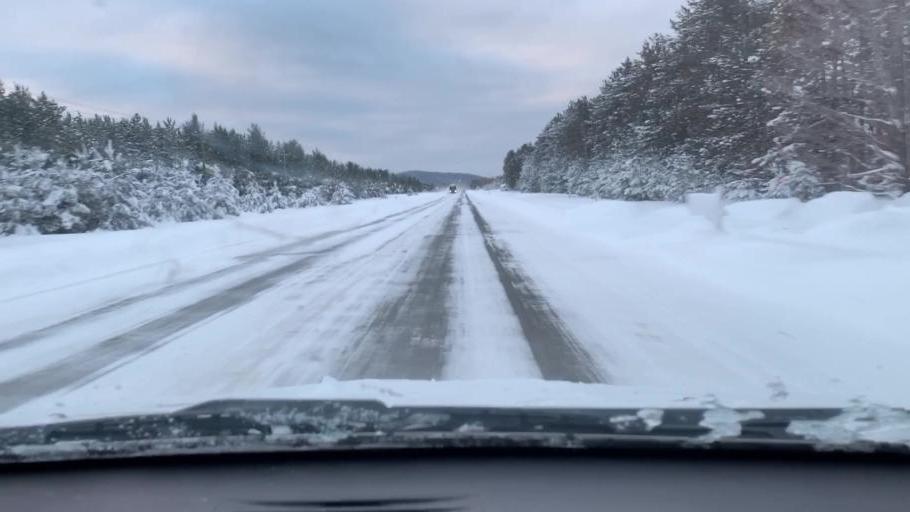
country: US
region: Michigan
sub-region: Antrim County
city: Mancelona
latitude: 44.9244
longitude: -85.0509
